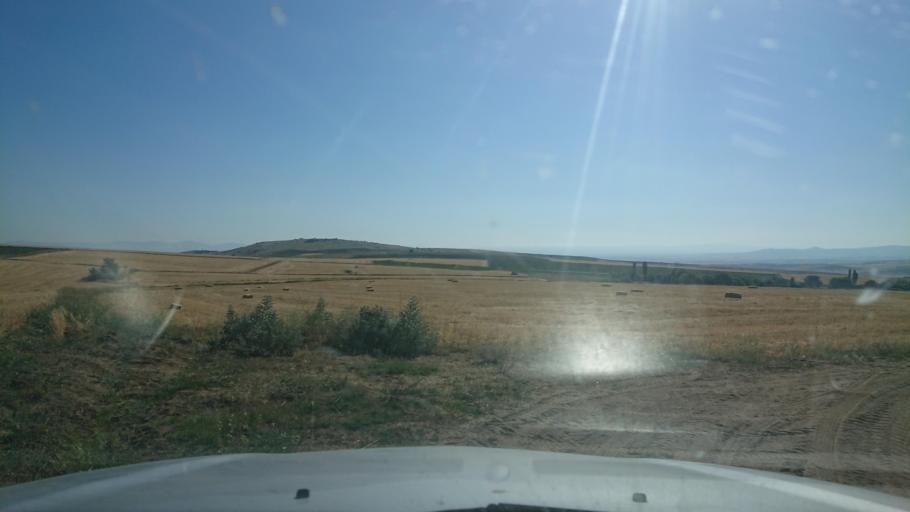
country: TR
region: Aksaray
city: Agacoren
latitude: 38.8352
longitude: 33.9472
